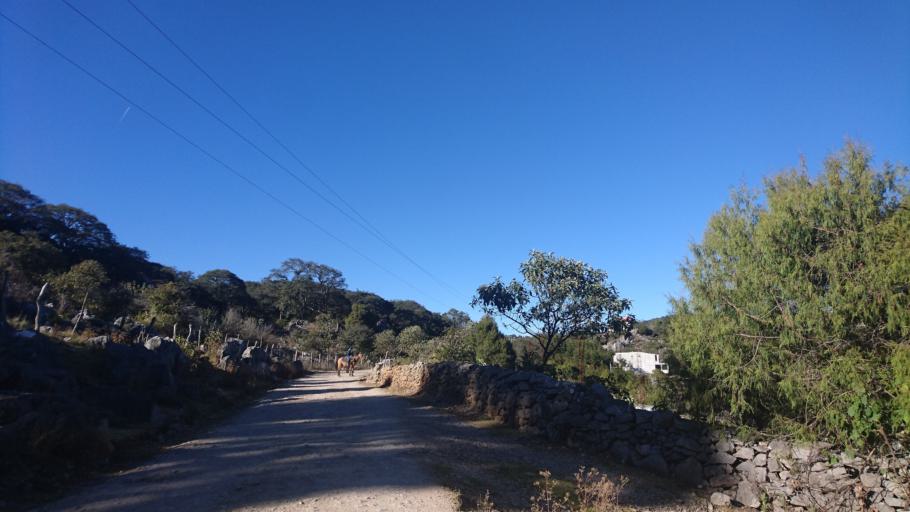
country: MX
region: San Luis Potosi
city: Zaragoza
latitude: 22.0255
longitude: -100.6027
